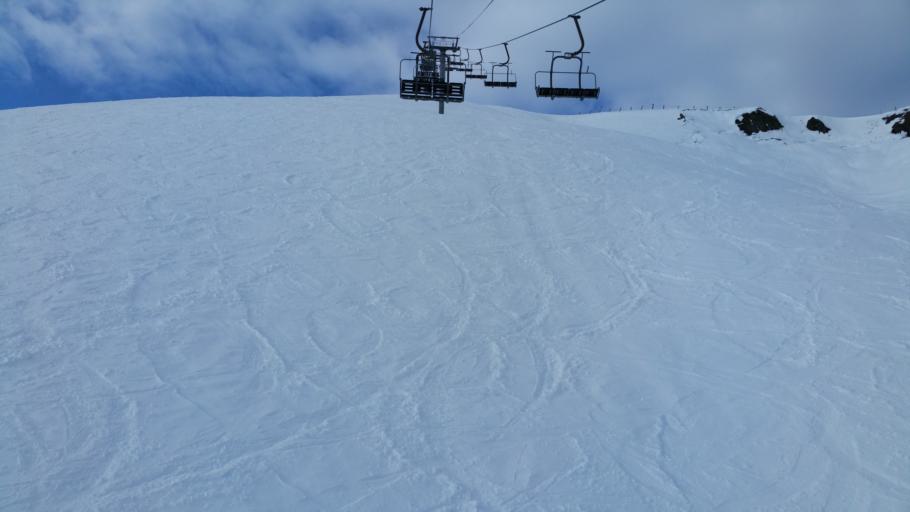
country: FR
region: Rhone-Alpes
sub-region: Departement de la Savoie
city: Saint-Etienne-de-Cuines
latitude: 45.2703
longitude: 6.2599
